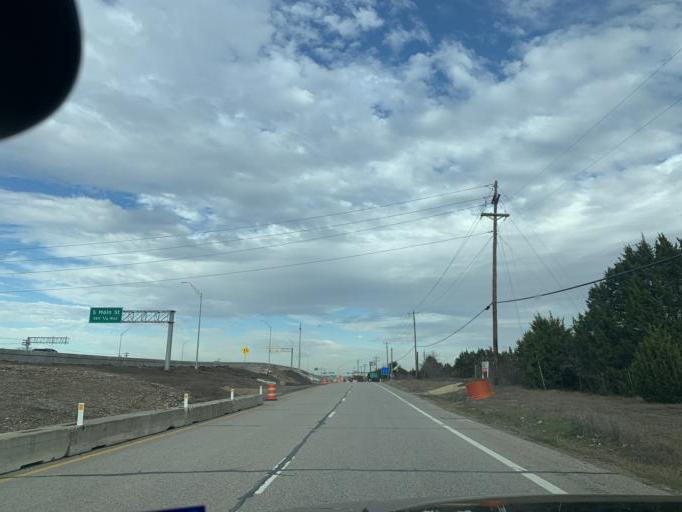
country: US
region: Texas
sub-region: Dallas County
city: Shamrock
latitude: 32.6168
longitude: -96.9165
